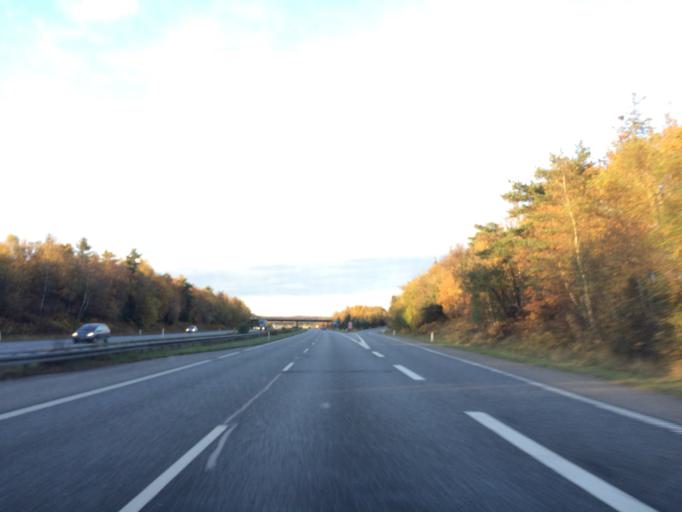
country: DK
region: South Denmark
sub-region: Aabenraa Kommune
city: Aabenraa
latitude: 54.9790
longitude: 9.3810
